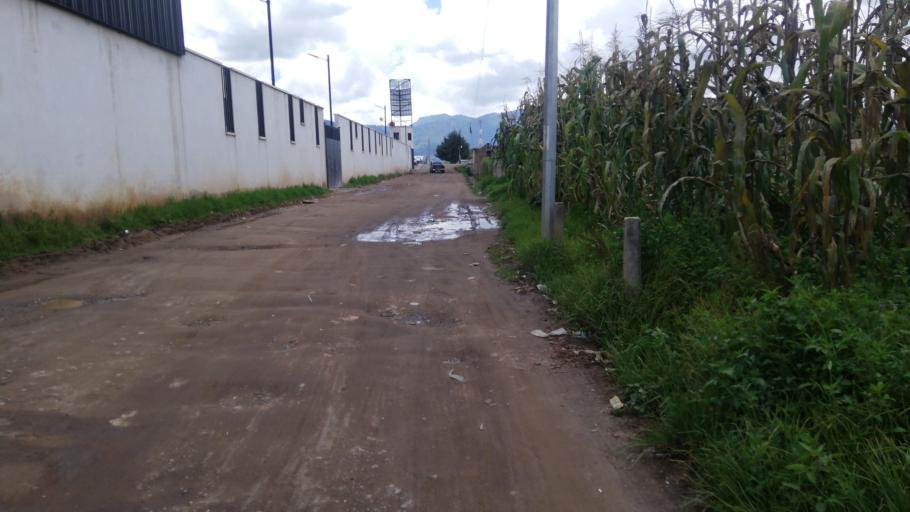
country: GT
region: Totonicapan
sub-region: Municipio de San Andres Xecul
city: San Andres Xecul
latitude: 14.8872
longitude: -91.4700
